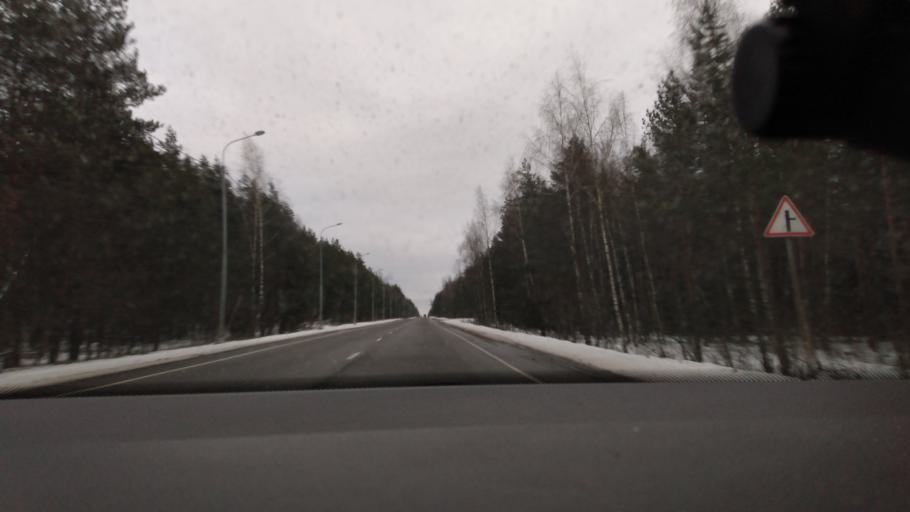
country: RU
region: Moskovskaya
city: Il'inskiy Pogost
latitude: 55.4722
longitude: 38.9587
